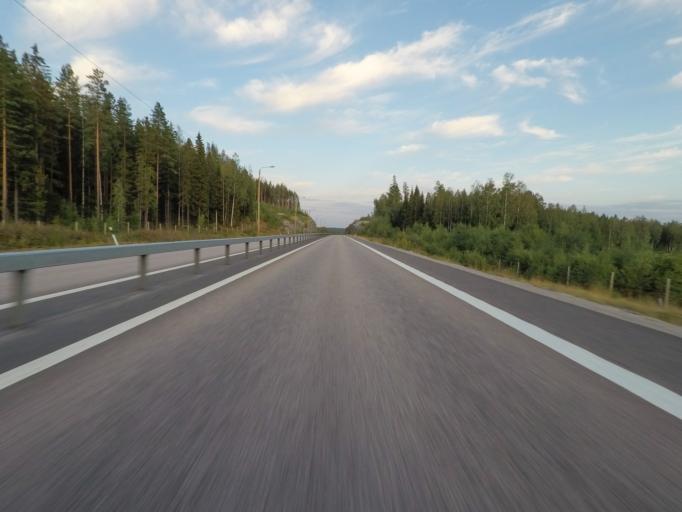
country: FI
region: Central Finland
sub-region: Jyvaeskylae
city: Toivakka
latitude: 62.0856
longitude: 26.0167
